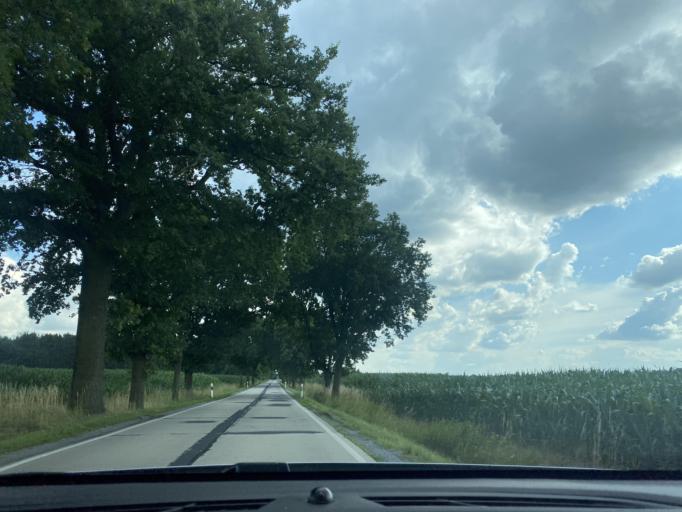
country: DE
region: Saxony
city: Klitten
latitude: 51.3590
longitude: 14.6077
